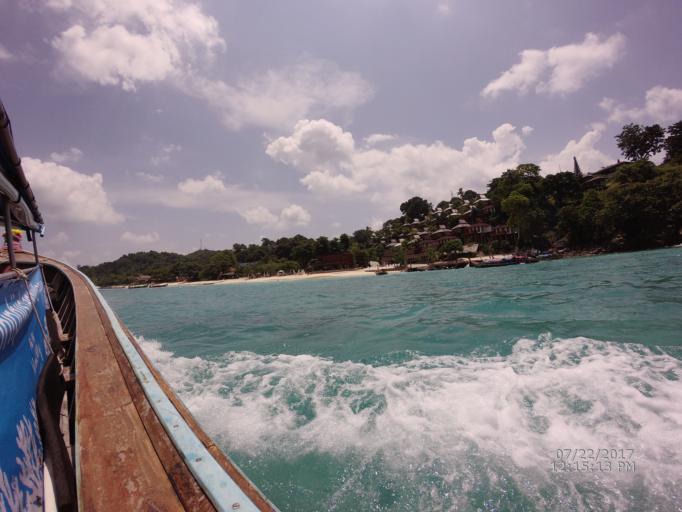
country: TH
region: Krabi
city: Saladan
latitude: 7.7270
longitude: 98.7884
